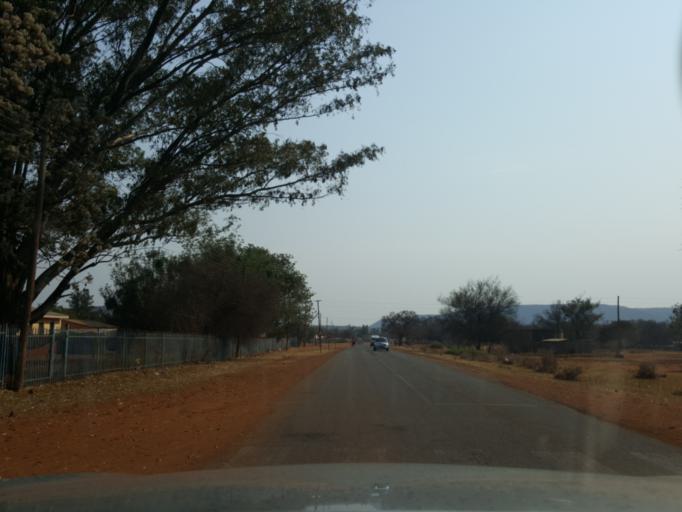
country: BW
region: South East
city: Lobatse
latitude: -25.3182
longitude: 25.7958
